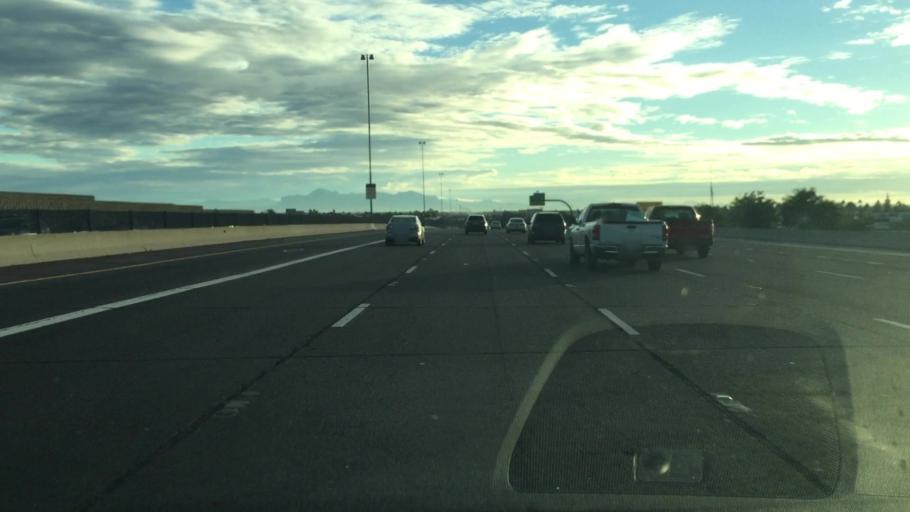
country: US
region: Arizona
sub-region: Maricopa County
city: Mesa
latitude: 33.3845
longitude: -111.8304
